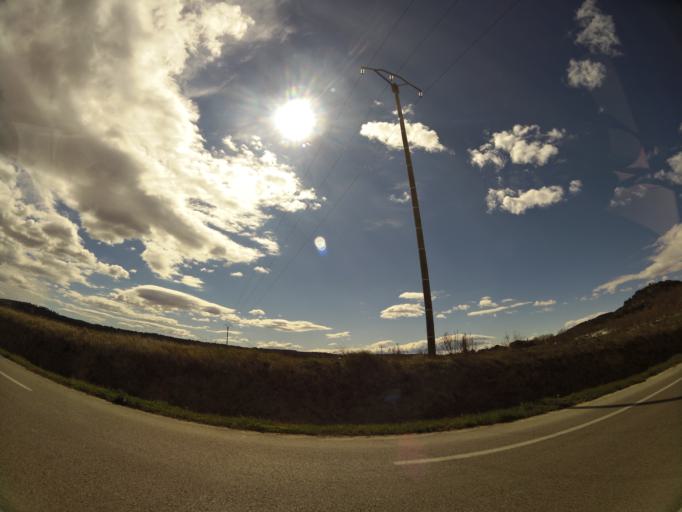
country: FR
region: Languedoc-Roussillon
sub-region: Departement du Gard
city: Calvisson
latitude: 43.7784
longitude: 4.1960
